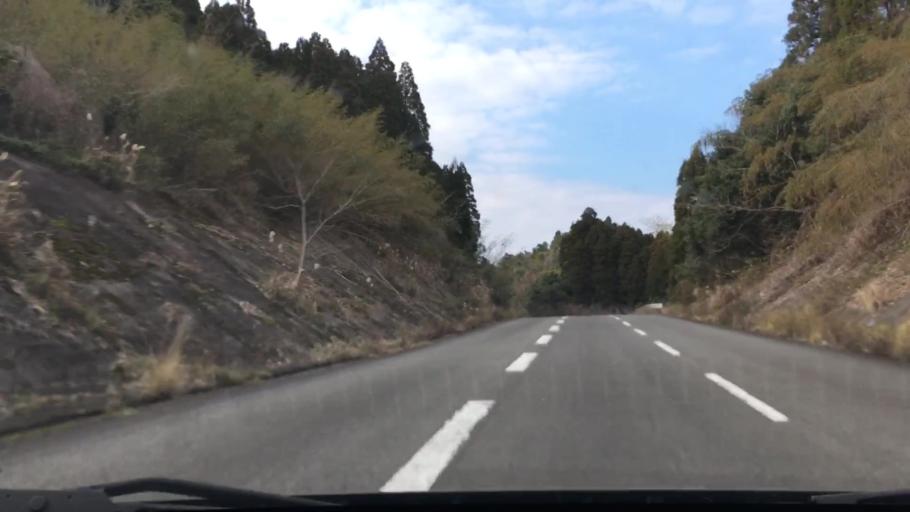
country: JP
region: Miyazaki
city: Nichinan
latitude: 31.6361
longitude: 131.3364
